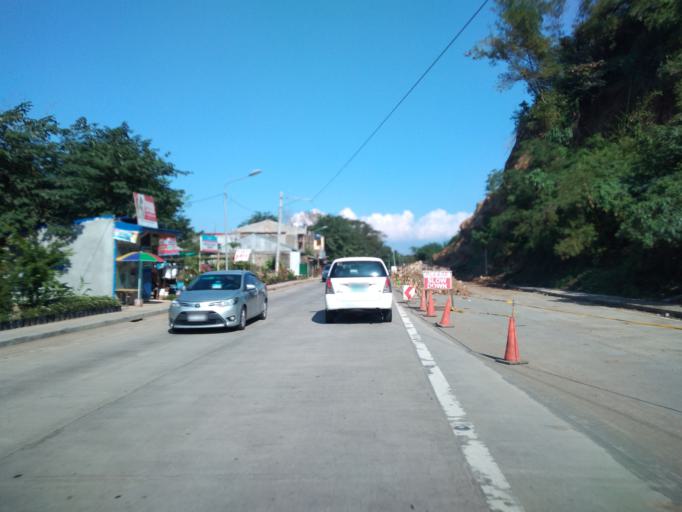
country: PH
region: Calabarzon
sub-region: Province of Laguna
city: Calamba
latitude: 14.1857
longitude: 121.1659
